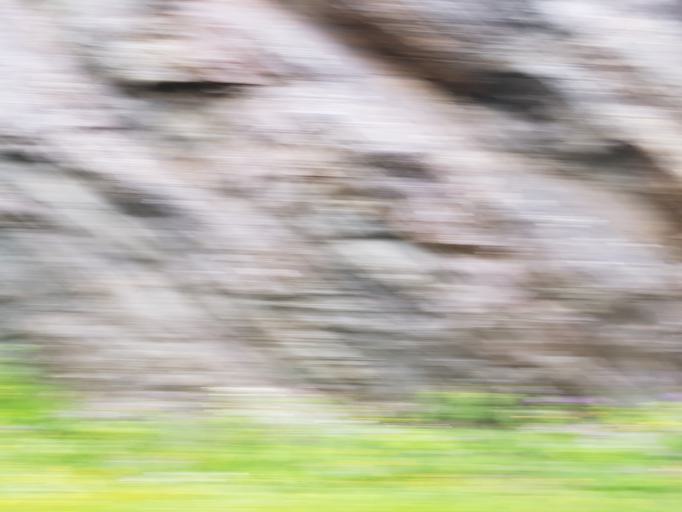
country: NO
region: Sor-Trondelag
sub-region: Selbu
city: Mebonden
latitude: 63.3195
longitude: 11.0842
